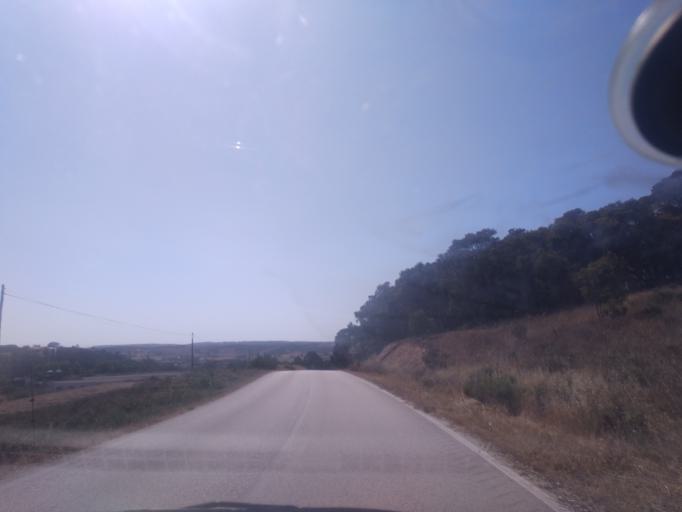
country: PT
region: Faro
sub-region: Aljezur
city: Aljezur
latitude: 37.2257
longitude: -8.8123
